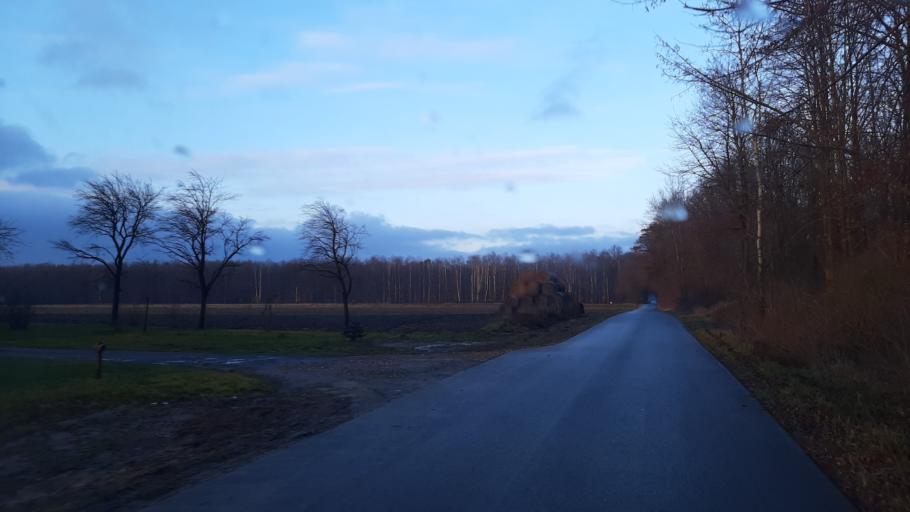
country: PL
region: Lublin Voivodeship
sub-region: Powiat lubelski
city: Garbow
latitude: 51.3711
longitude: 22.3994
